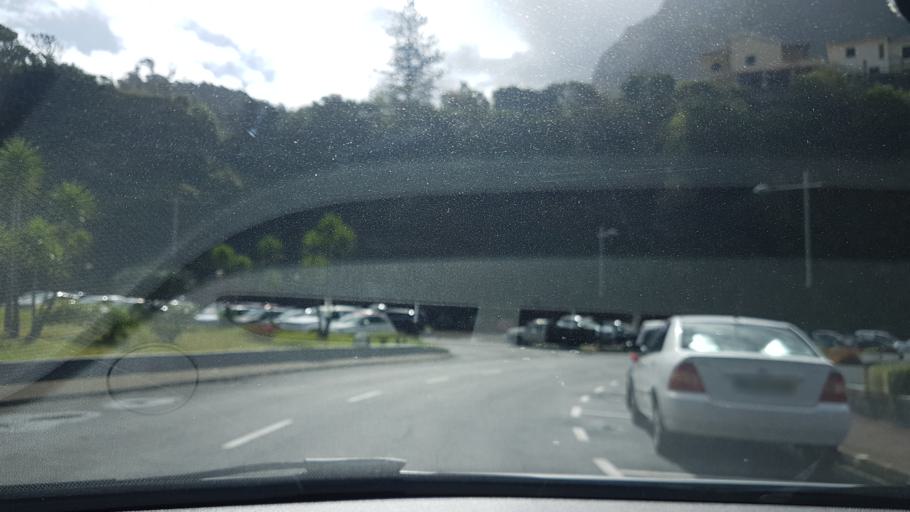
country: PT
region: Madeira
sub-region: Sao Vicente
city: Sao Vicente
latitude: 32.8032
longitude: -17.0456
